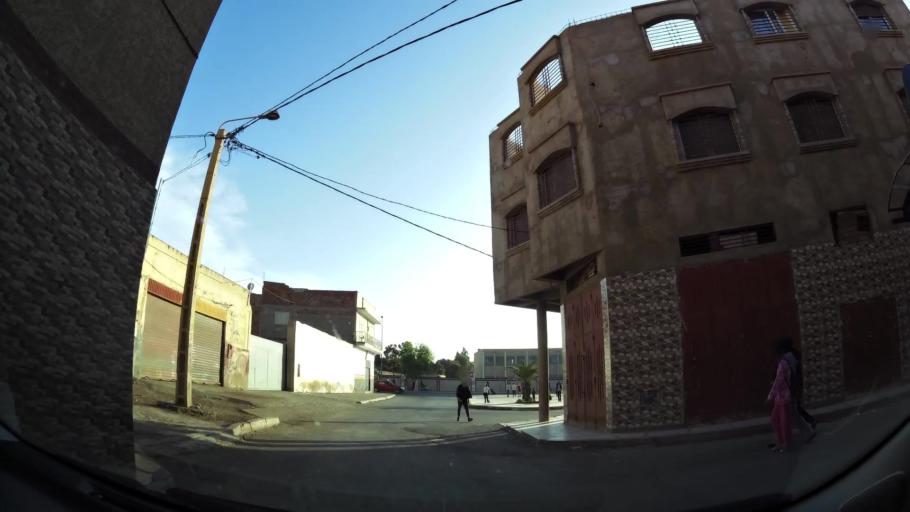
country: MA
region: Oriental
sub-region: Oujda-Angad
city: Oujda
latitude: 34.7001
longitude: -1.9107
